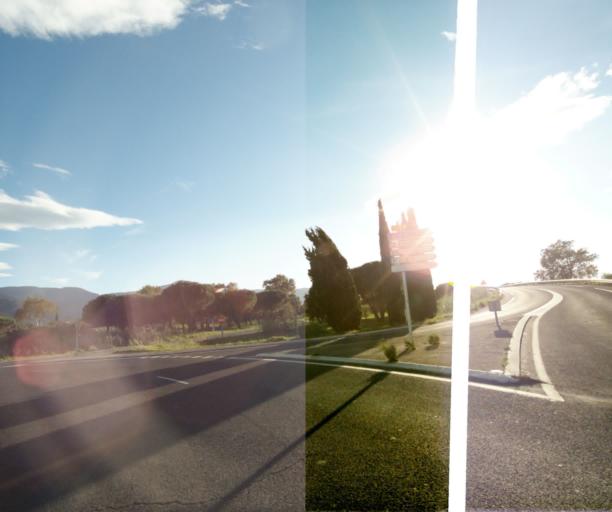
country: FR
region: Languedoc-Roussillon
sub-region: Departement des Pyrenees-Orientales
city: Argelers
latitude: 42.5645
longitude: 3.0068
